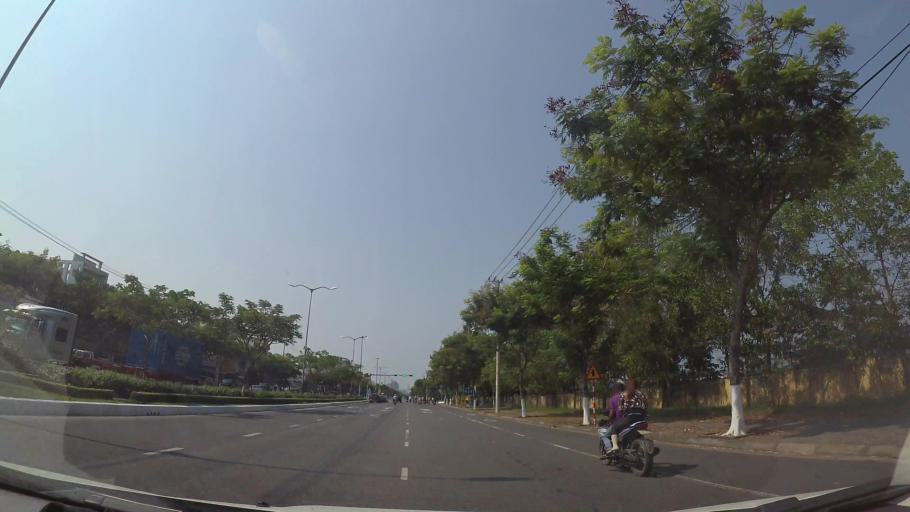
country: VN
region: Da Nang
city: Ngu Hanh Son
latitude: 16.0309
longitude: 108.2469
